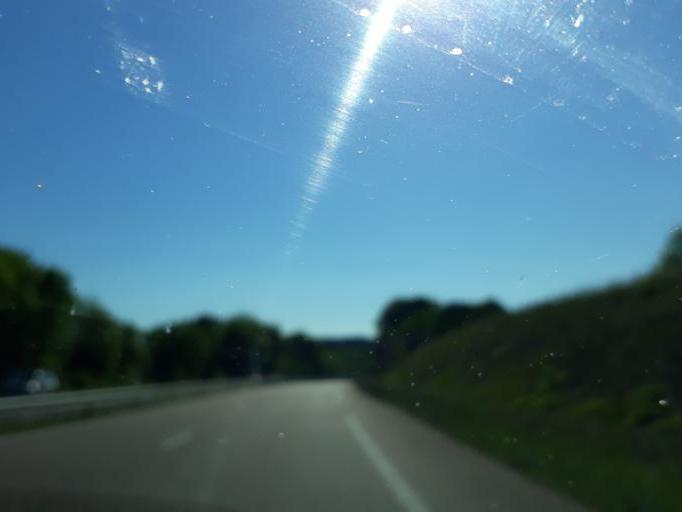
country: FR
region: Bourgogne
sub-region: Departement de la Cote-d'Or
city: Pouilly-en-Auxois
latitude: 47.2739
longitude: 4.6035
